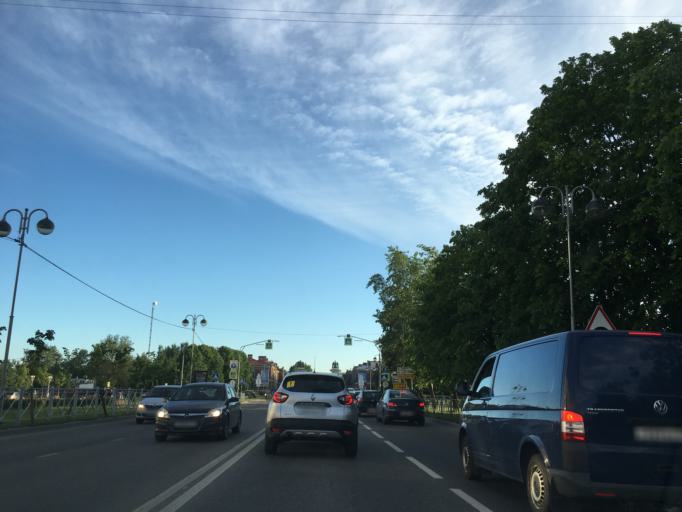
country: RU
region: Leningrad
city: Gatchina
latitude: 59.5777
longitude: 30.1342
